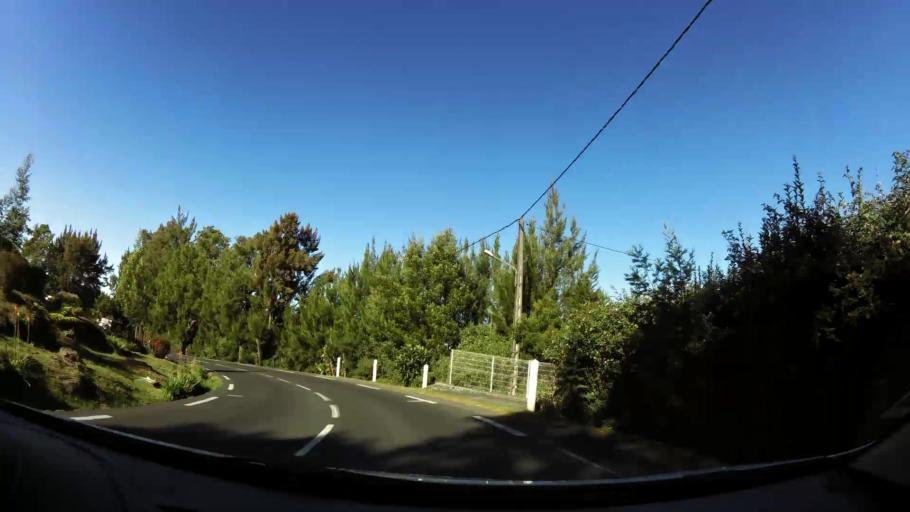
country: RE
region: Reunion
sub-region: Reunion
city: Le Tampon
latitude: -21.2274
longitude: 55.5509
